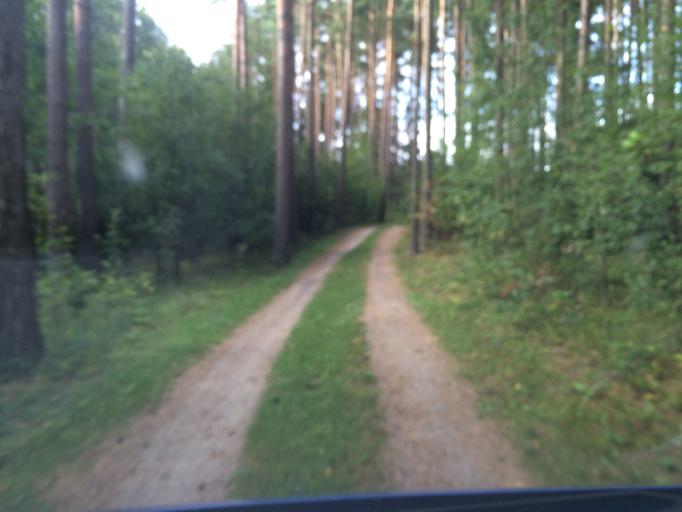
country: NO
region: Ostfold
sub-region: Hvaler
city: Skjaerhalden
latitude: 59.0361
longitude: 11.0098
